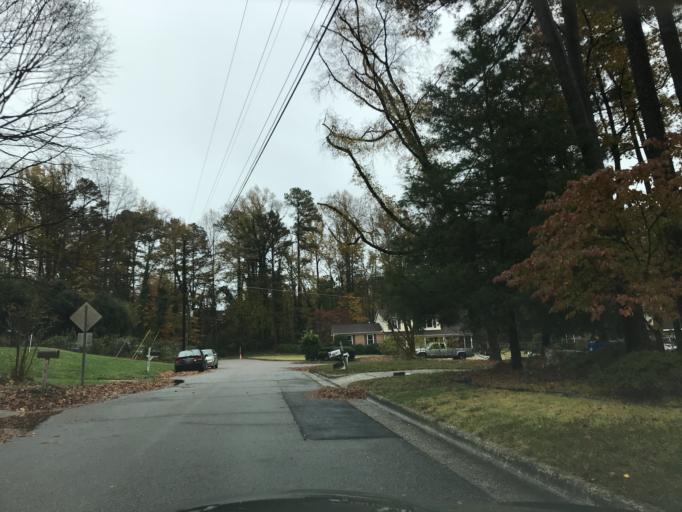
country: US
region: North Carolina
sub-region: Wake County
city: West Raleigh
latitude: 35.8354
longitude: -78.6210
